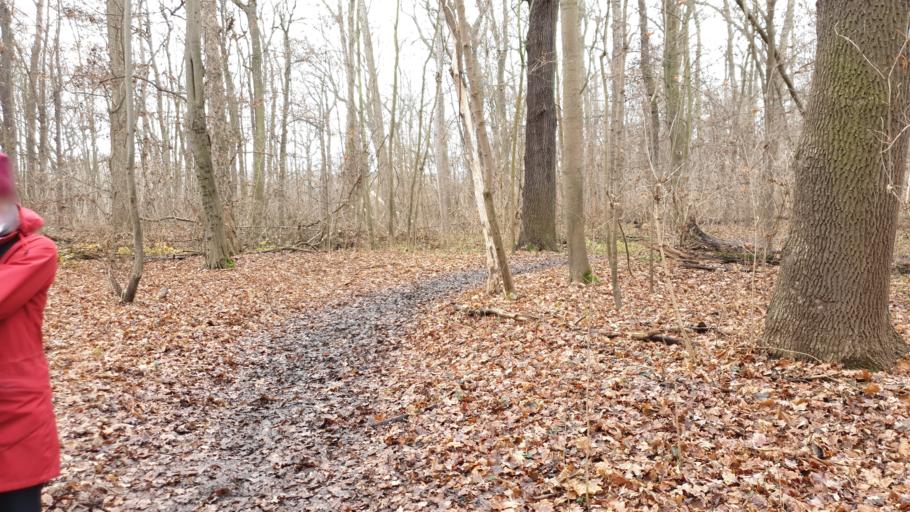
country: DE
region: Saxony
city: Schkeuditz
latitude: 51.3683
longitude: 12.2878
